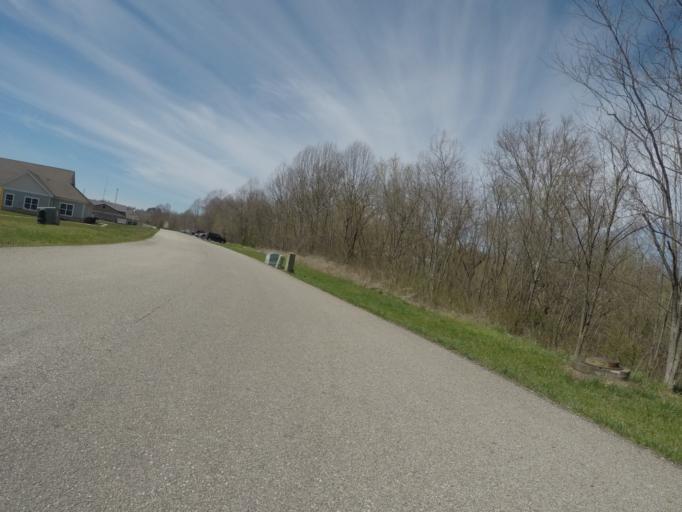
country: US
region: West Virginia
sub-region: Cabell County
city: Pea Ridge
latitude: 38.4106
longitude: -82.3082
